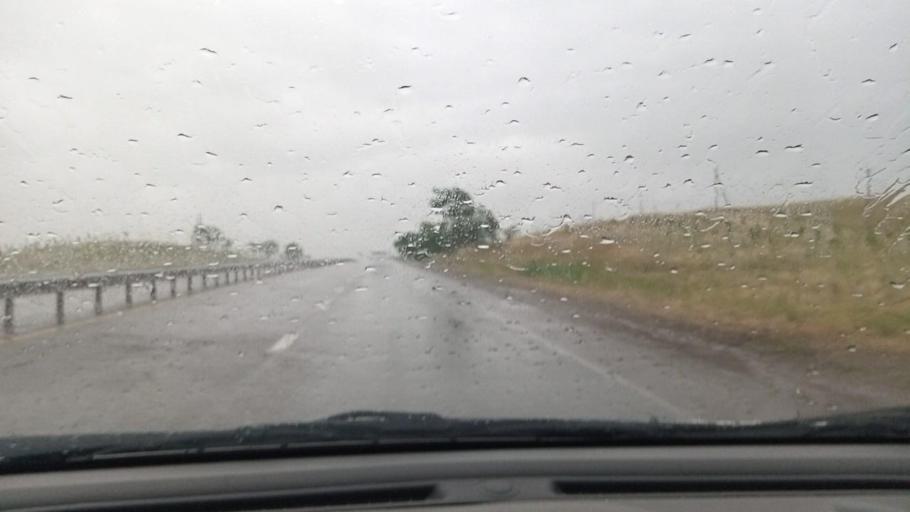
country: UZ
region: Toshkent
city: Ohangaron
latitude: 40.9654
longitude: 69.5527
